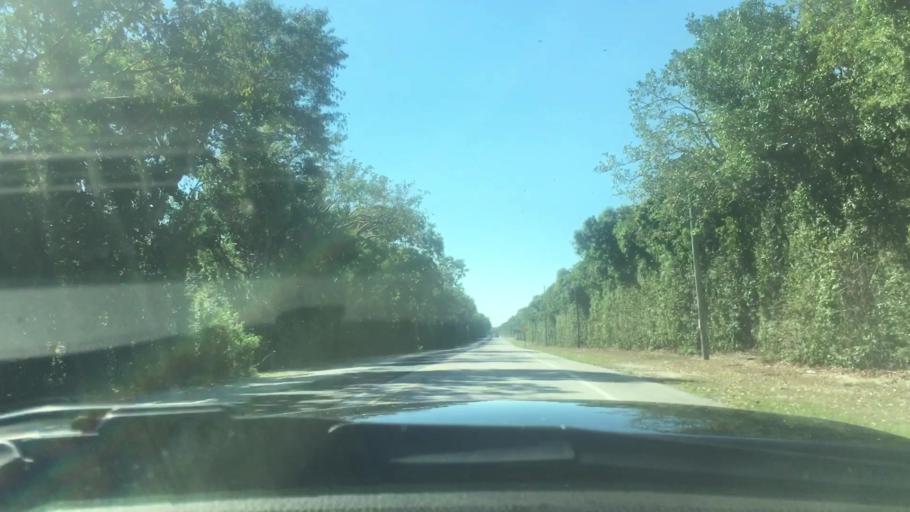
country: US
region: Florida
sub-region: Monroe County
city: North Key Largo
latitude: 25.2389
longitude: -80.3229
